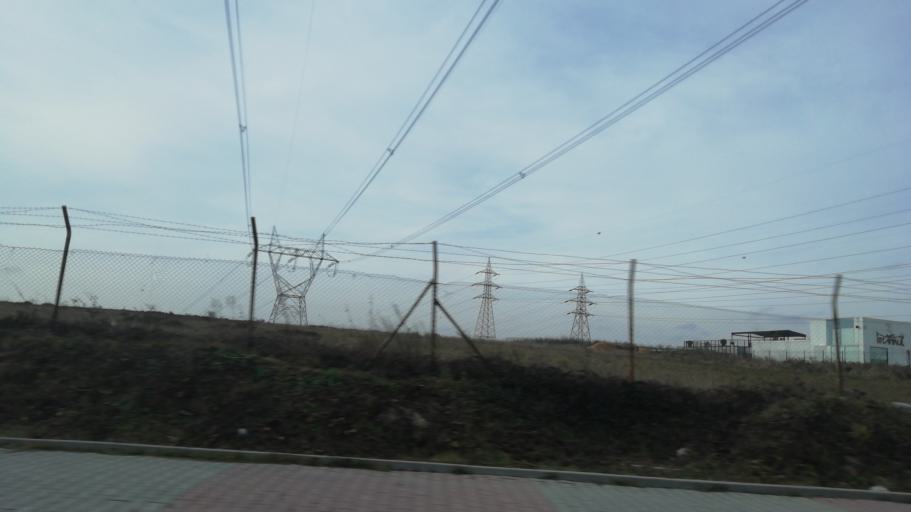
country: TR
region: Istanbul
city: Basaksehir
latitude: 41.1166
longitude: 28.7987
